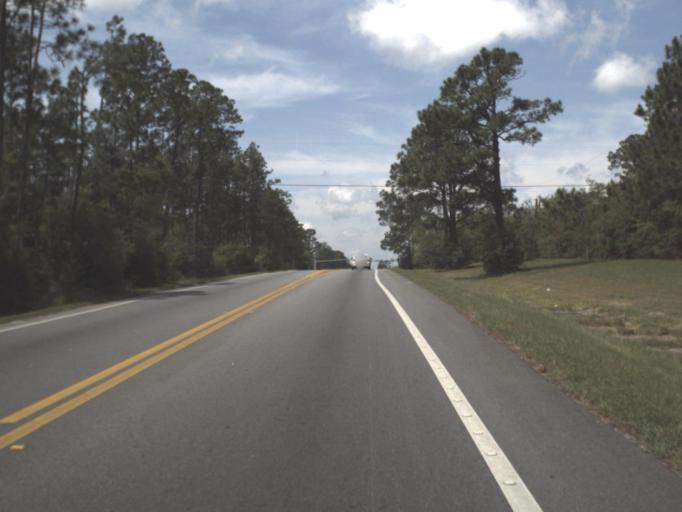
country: US
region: Florida
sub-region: Escambia County
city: Cantonment
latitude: 30.5350
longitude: -87.3503
